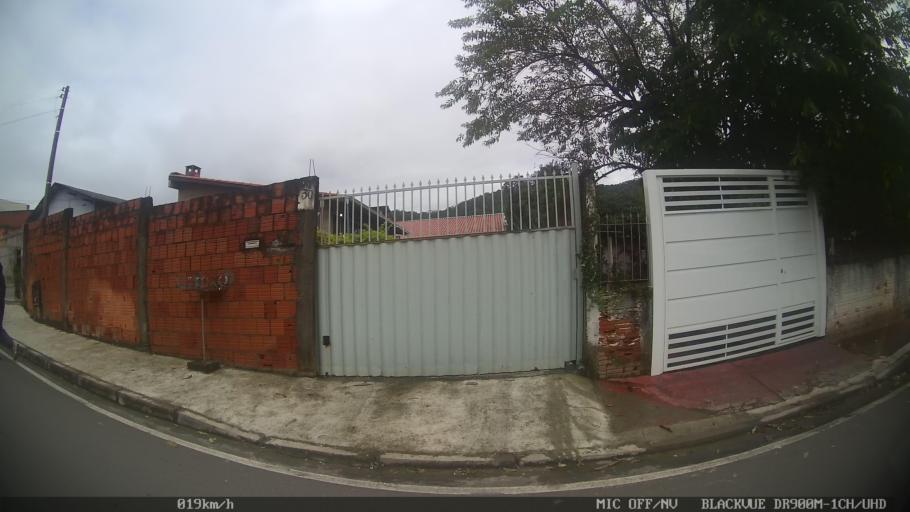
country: BR
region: Santa Catarina
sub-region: Biguacu
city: Biguacu
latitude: -27.5439
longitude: -48.6450
